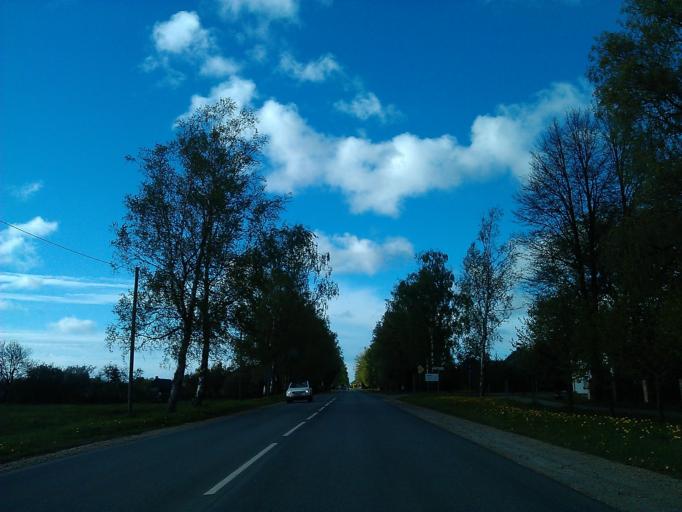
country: LV
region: Adazi
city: Adazi
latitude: 57.0719
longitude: 24.3209
